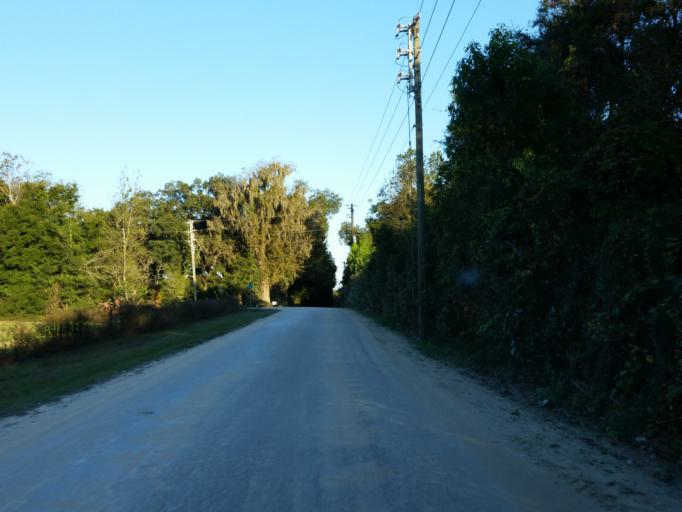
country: US
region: Florida
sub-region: Hernando County
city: Hill 'n Dale
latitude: 28.4568
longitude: -82.2542
